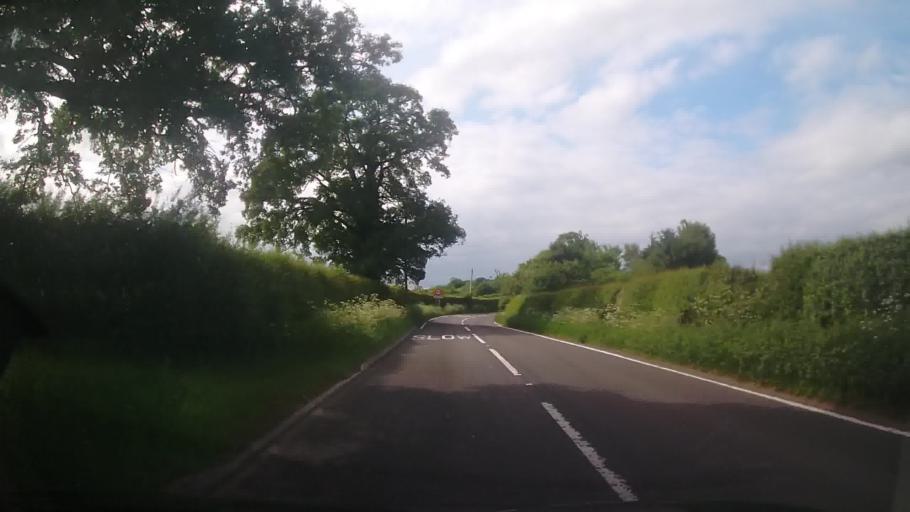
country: GB
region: England
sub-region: Shropshire
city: Petton
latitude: 52.8260
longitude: -2.8044
